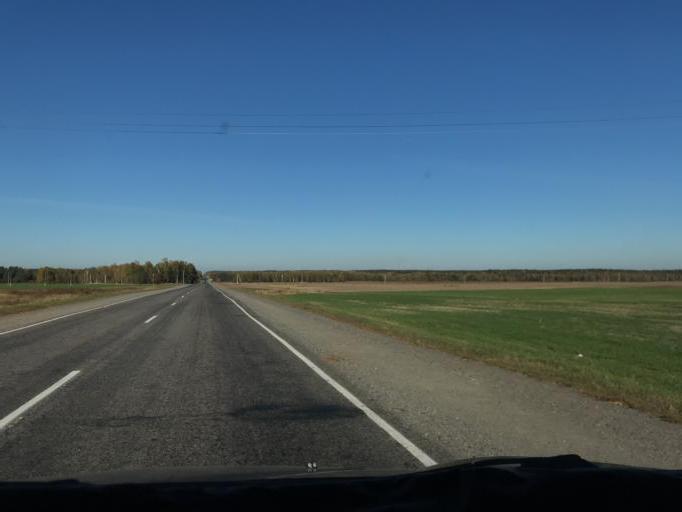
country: BY
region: Gomel
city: Yel'sk
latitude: 51.7757
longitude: 29.1914
